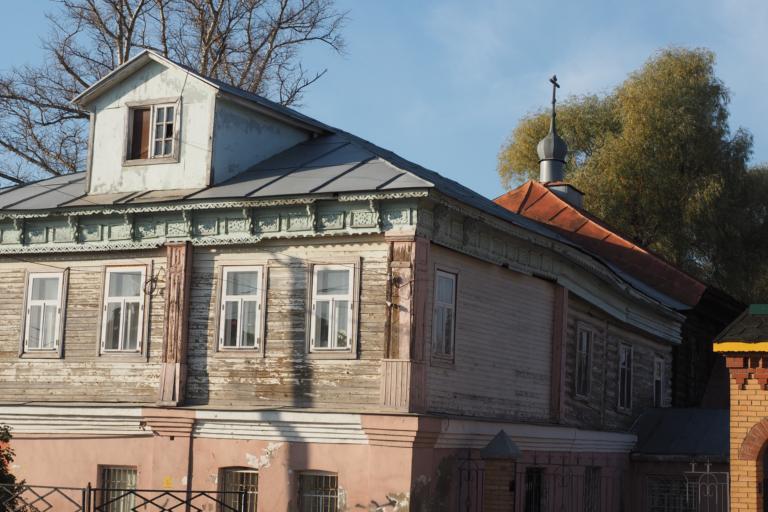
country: RU
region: Moskovskaya
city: Kurovskoye
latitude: 55.5786
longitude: 38.9128
